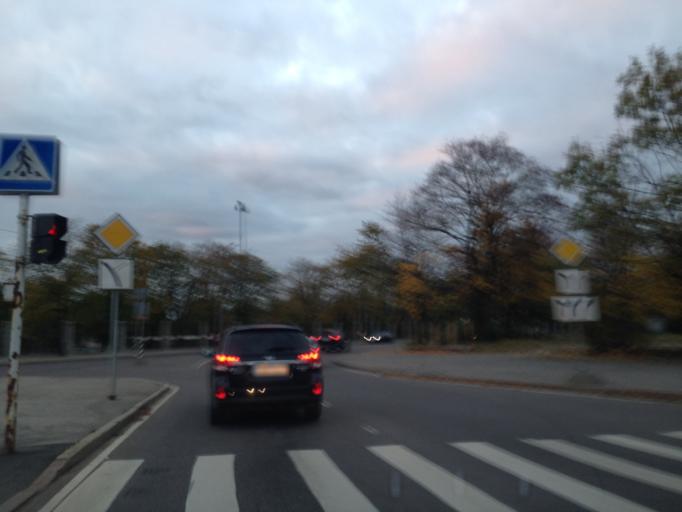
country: EE
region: Harju
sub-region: Tallinna linn
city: Tallinn
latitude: 59.4261
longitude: 24.8007
